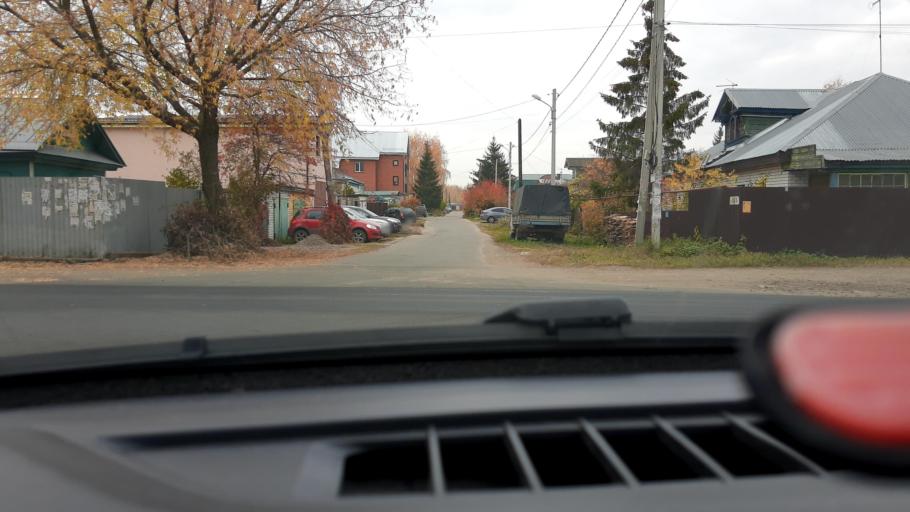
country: RU
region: Nizjnij Novgorod
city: Gorbatovka
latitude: 56.3314
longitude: 43.8309
